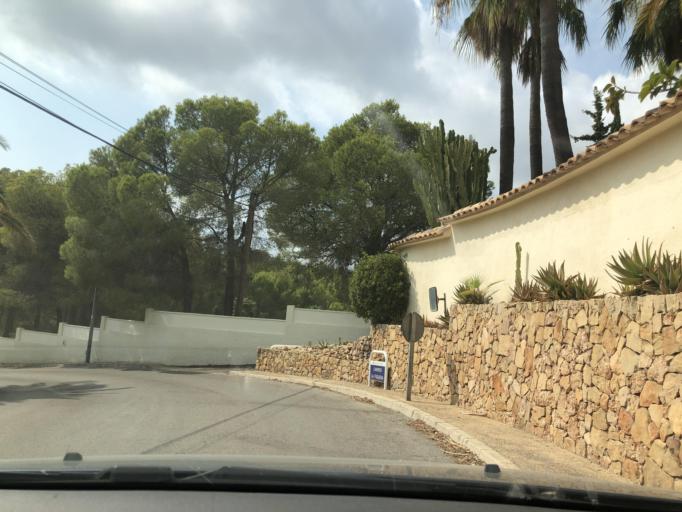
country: ES
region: Valencia
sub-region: Provincia de Alicante
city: Altea
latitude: 38.6355
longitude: -0.0683
